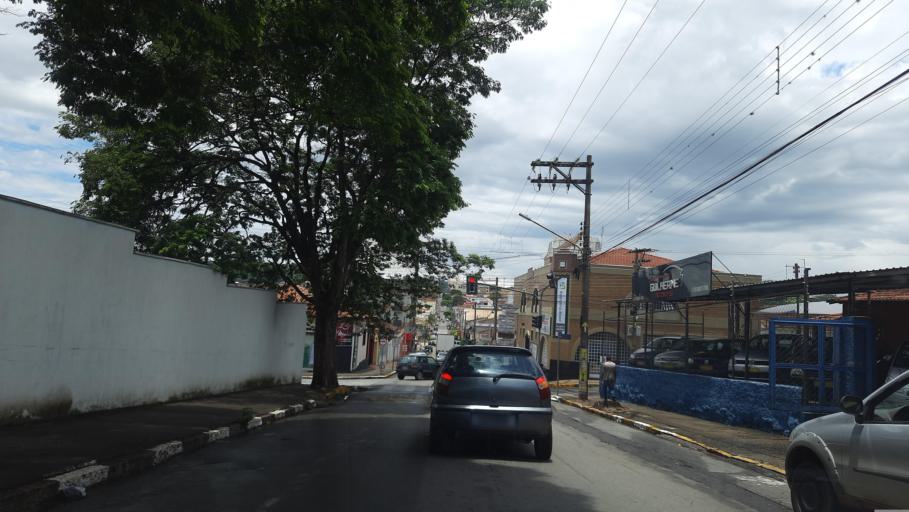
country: BR
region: Sao Paulo
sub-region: Vargem Grande Do Sul
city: Vargem Grande do Sul
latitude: -21.8373
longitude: -46.8975
